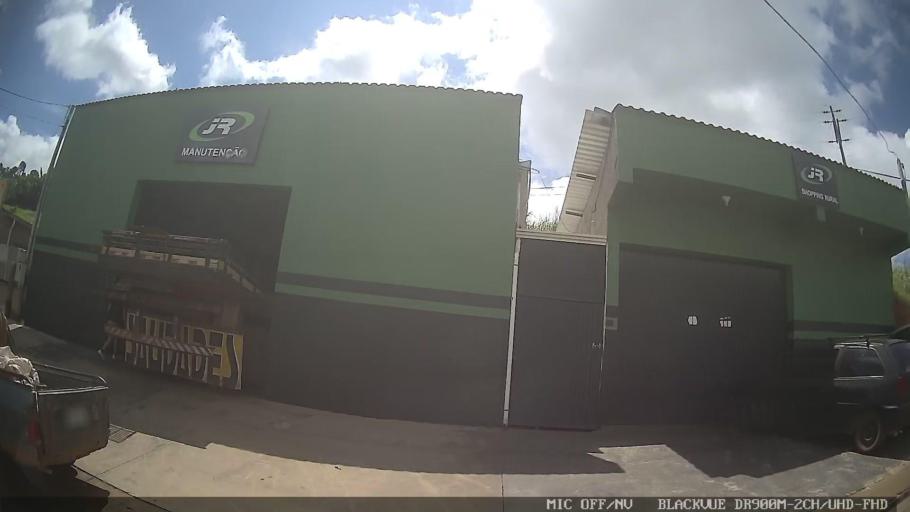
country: BR
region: Minas Gerais
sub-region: Extrema
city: Extrema
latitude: -22.8017
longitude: -46.4461
